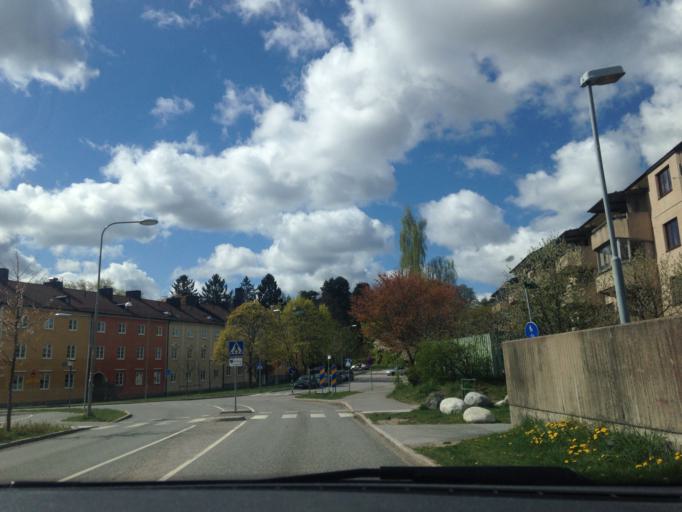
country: SE
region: Stockholm
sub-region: Stockholms Kommun
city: Arsta
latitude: 59.2849
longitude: 18.0991
